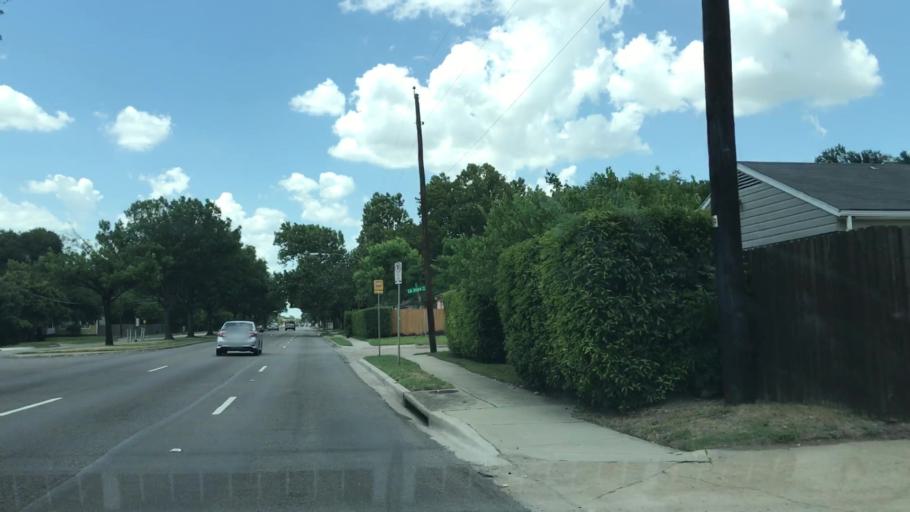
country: US
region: Texas
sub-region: Dallas County
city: University Park
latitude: 32.8719
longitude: -96.8561
